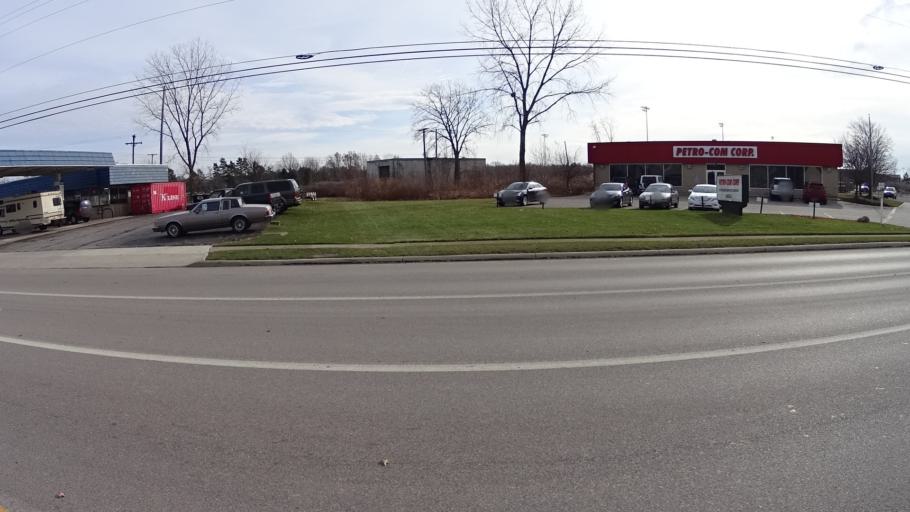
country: US
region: Ohio
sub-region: Lorain County
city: North Ridgeville
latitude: 41.3845
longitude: -81.9780
